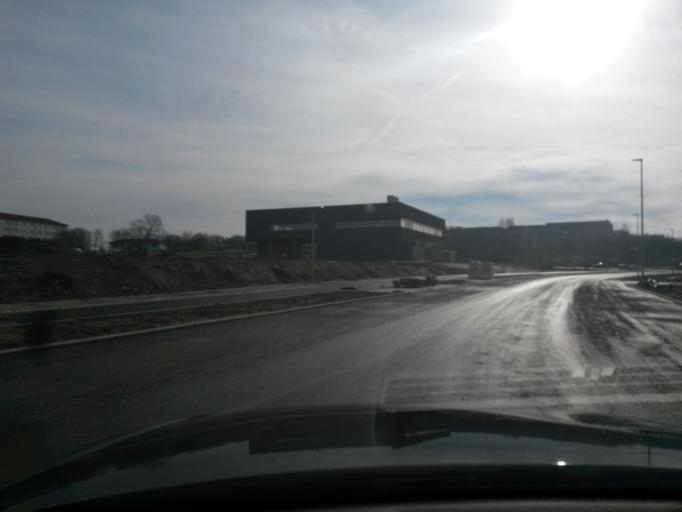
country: DE
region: Bavaria
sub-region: Regierungsbezirk Unterfranken
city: Wuerzburg
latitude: 49.7867
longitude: 9.9684
